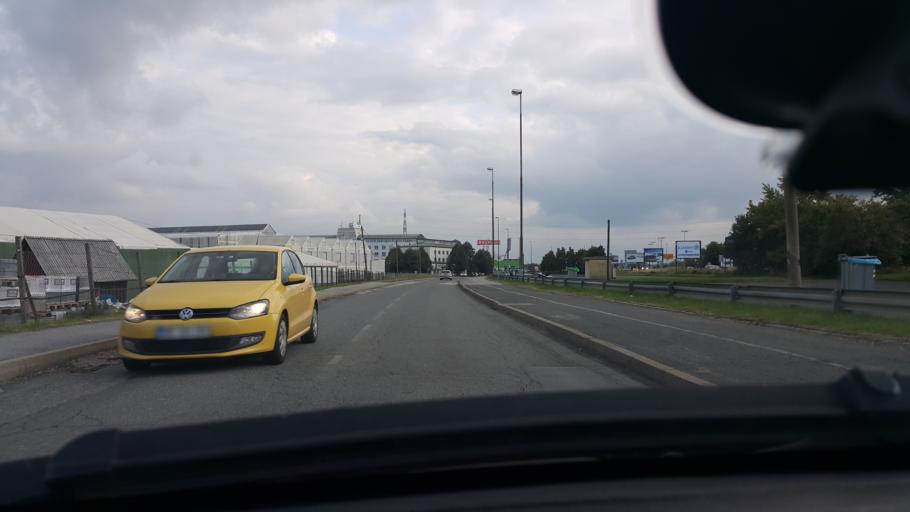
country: SI
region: Maribor
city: Razvanje
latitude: 46.5282
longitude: 15.6474
